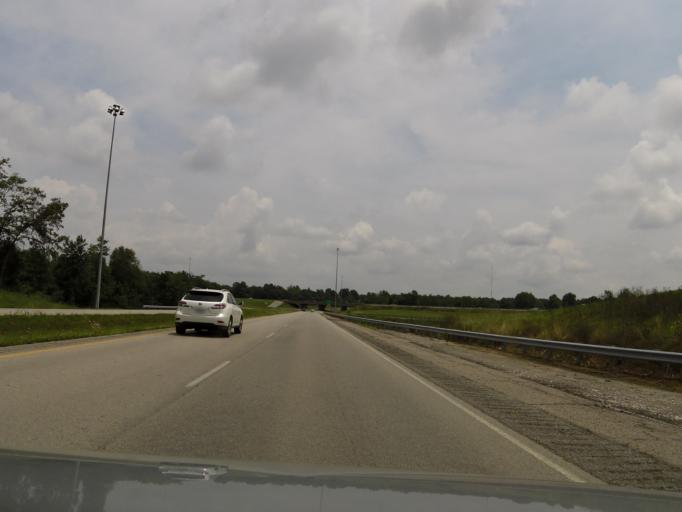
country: US
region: Kentucky
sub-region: Hardin County
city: Elizabethtown
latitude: 37.6771
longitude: -85.8654
